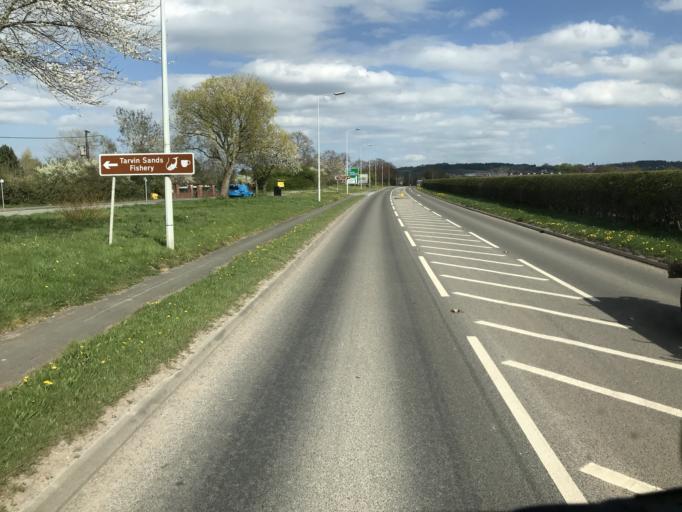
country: GB
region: England
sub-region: Cheshire West and Chester
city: Tarvin
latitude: 53.2062
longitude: -2.7510
